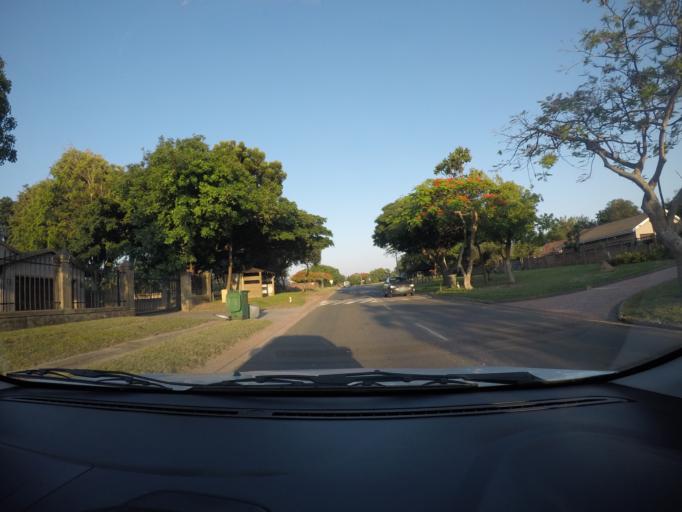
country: ZA
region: KwaZulu-Natal
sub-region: uThungulu District Municipality
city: Richards Bay
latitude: -28.7765
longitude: 32.1043
